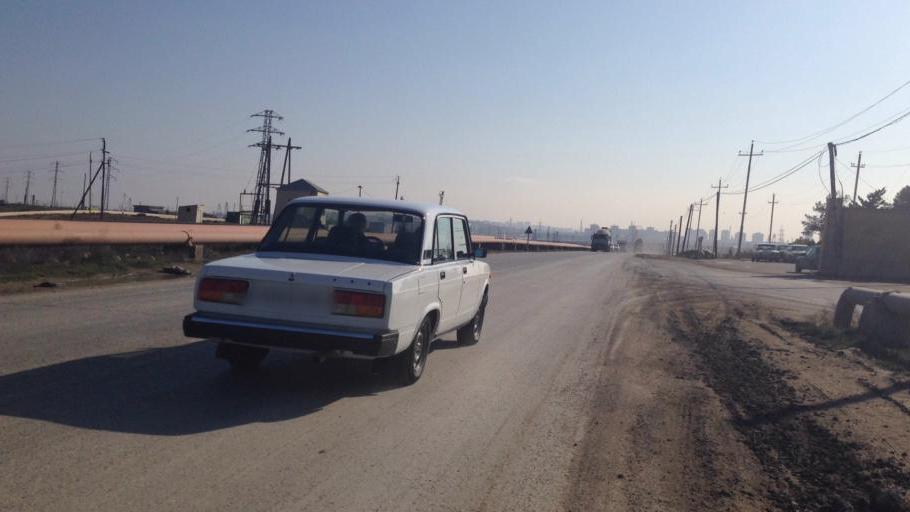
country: AZ
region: Baki
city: Balakhani
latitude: 40.4625
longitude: 49.8892
